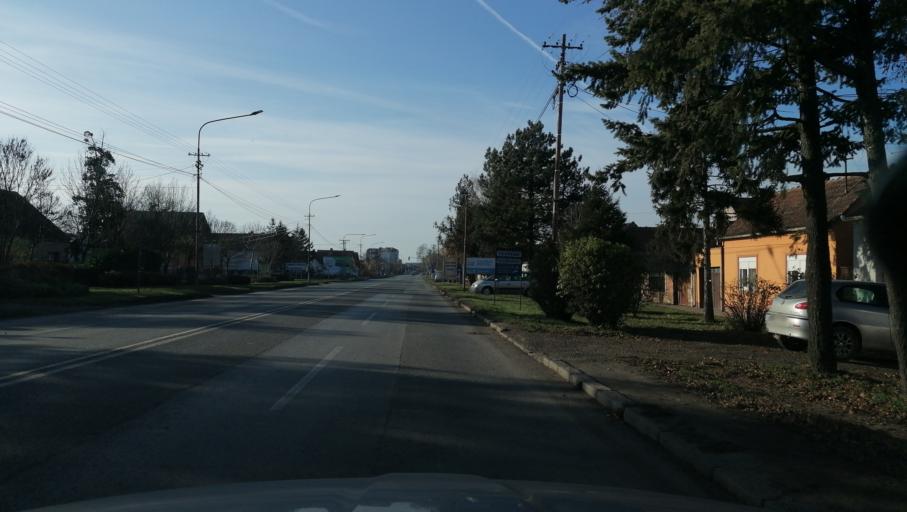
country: RS
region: Autonomna Pokrajina Vojvodina
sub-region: Sremski Okrug
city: Sremska Mitrovica
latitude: 44.9706
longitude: 19.6338
